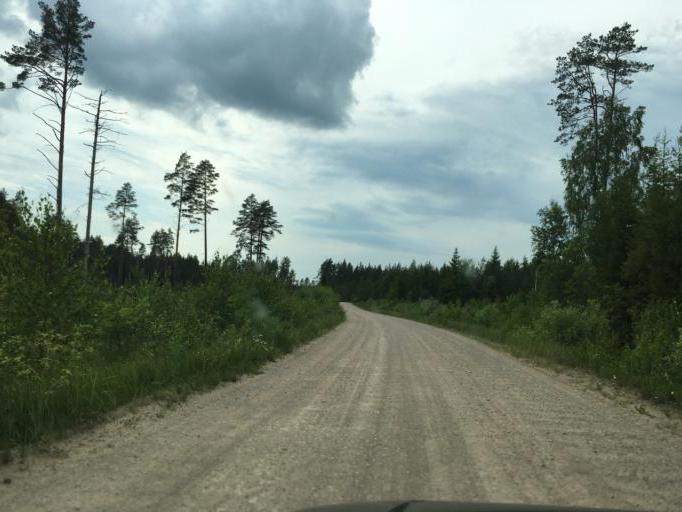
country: LV
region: Vilanu
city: Vilani
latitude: 56.7487
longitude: 27.0725
